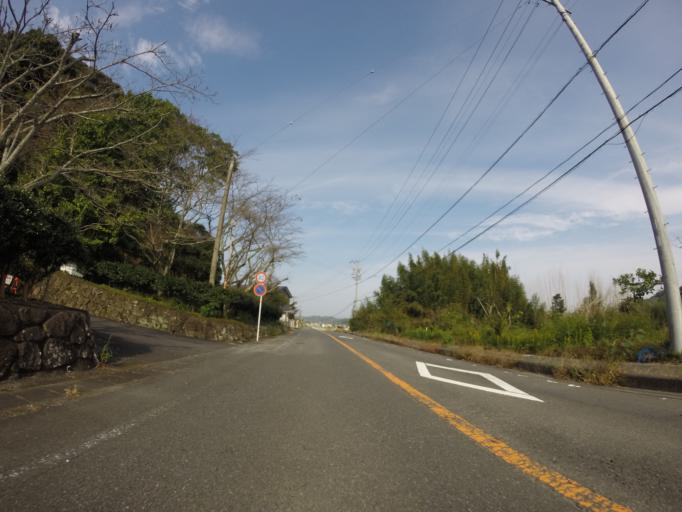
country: JP
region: Shizuoka
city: Shimada
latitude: 34.7617
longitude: 138.1904
